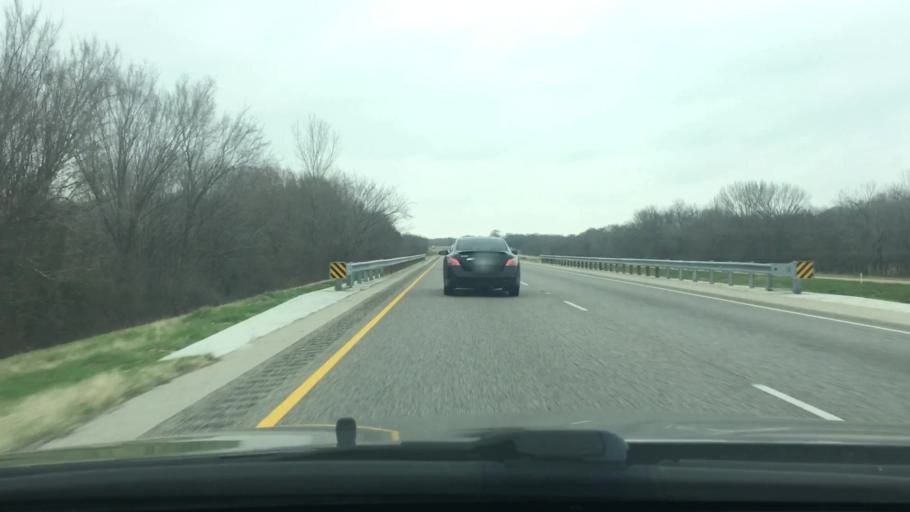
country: US
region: Texas
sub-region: Freestone County
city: Fairfield
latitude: 31.7988
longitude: -96.2568
